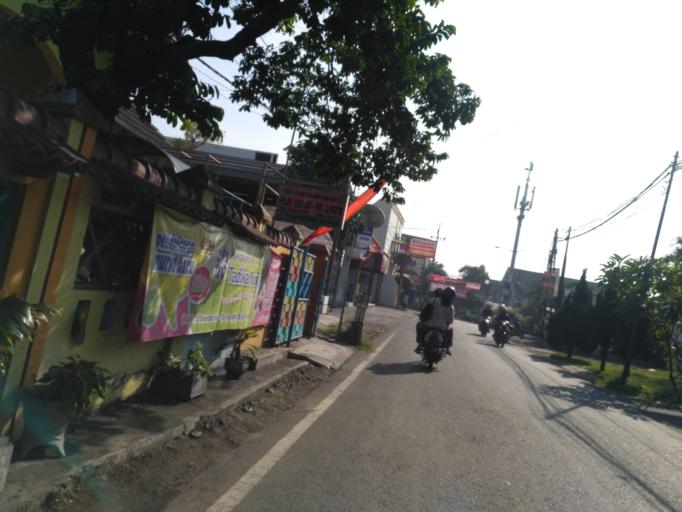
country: ID
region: East Java
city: Malang
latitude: -7.9482
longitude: 112.6243
